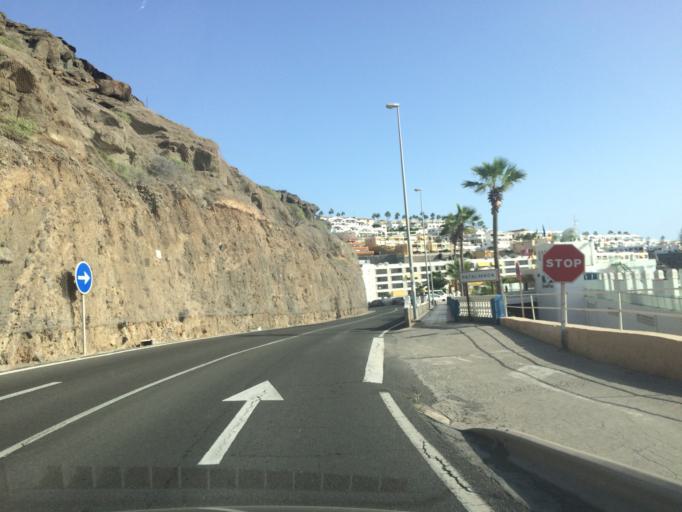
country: ES
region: Canary Islands
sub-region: Provincia de Las Palmas
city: Puerto Rico
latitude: 27.7719
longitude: -15.6897
